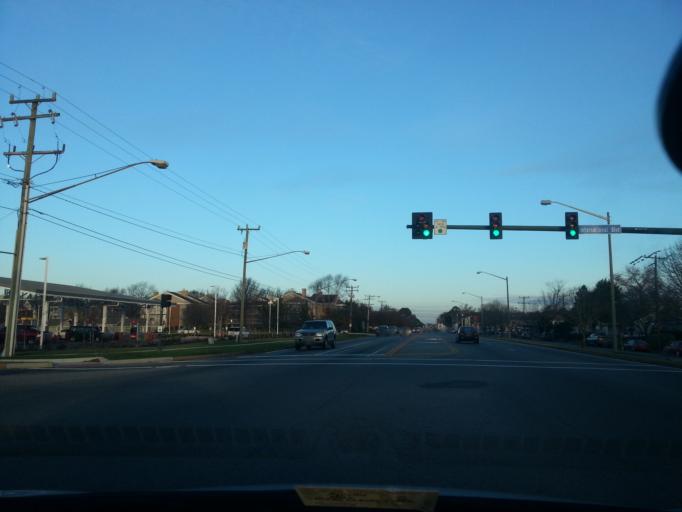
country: US
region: Virginia
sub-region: City of Norfolk
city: Norfolk
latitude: 36.8970
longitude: -76.2252
